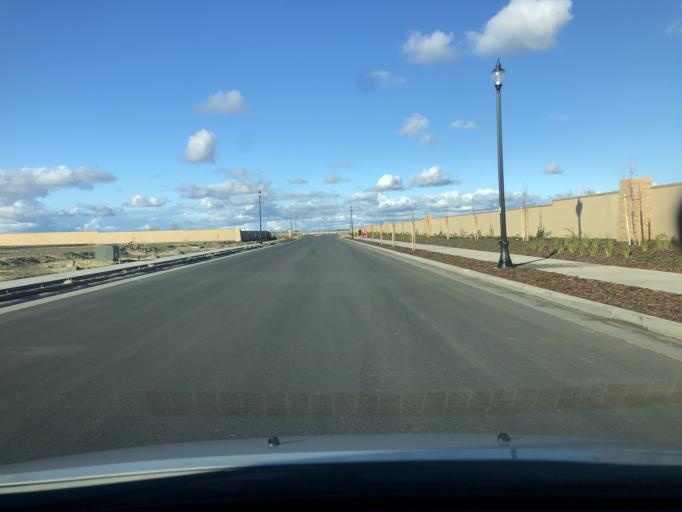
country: US
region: California
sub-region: Sacramento County
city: Elverta
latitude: 38.7723
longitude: -121.3967
